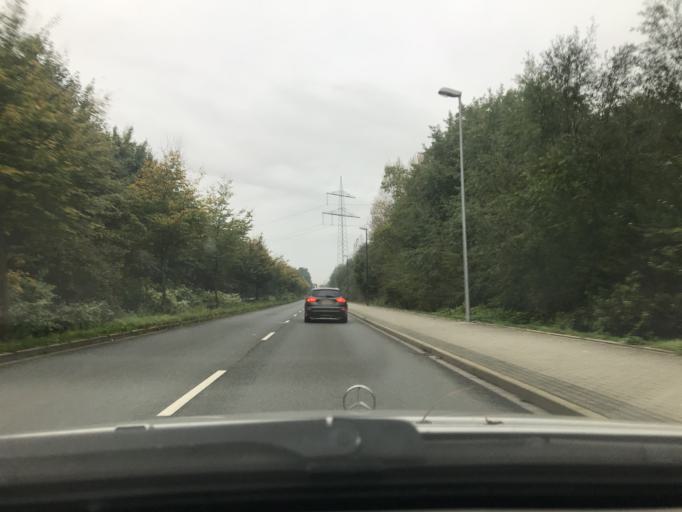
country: DE
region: North Rhine-Westphalia
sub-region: Regierungsbezirk Munster
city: Gelsenkirchen
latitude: 51.5381
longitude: 7.1020
